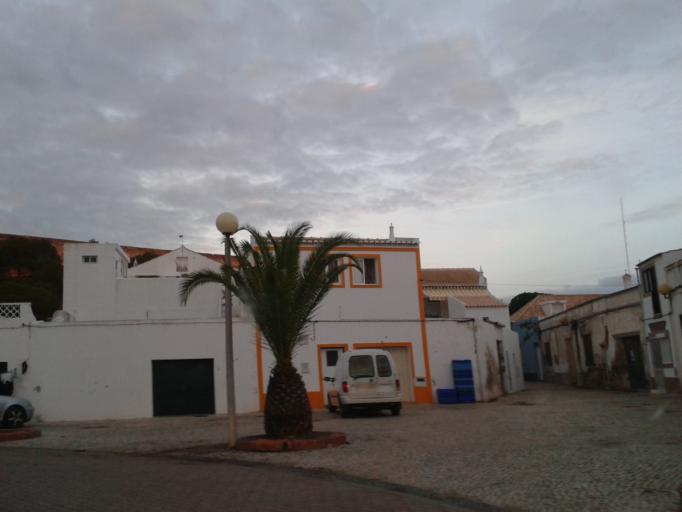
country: PT
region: Faro
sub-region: Castro Marim
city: Castro Marim
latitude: 37.2178
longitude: -7.4442
